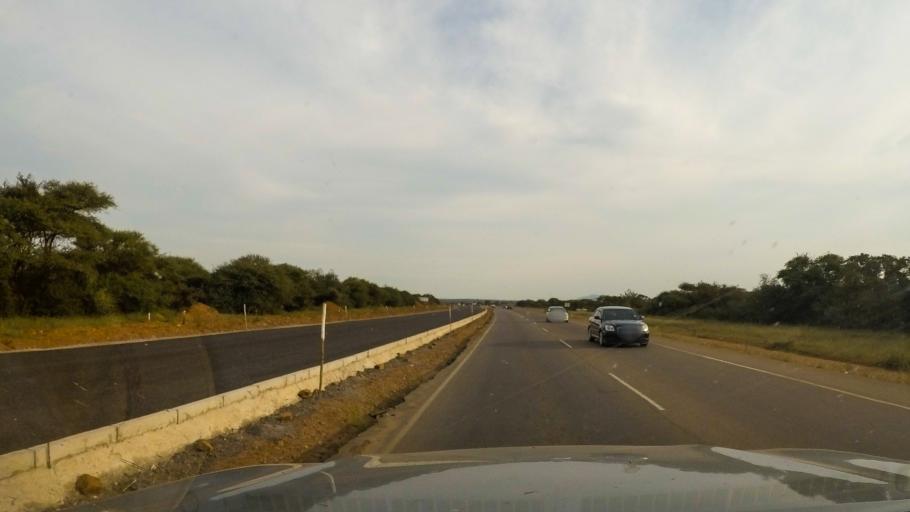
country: BW
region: South East
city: Ramotswa
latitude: -24.7752
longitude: 25.8266
